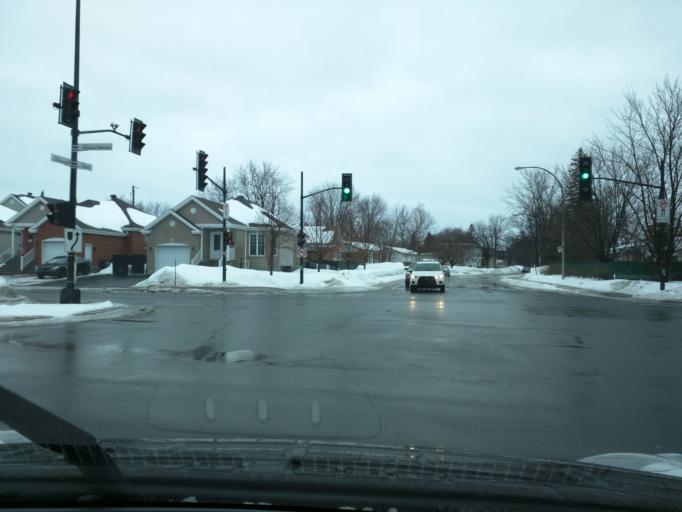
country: CA
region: Quebec
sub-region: Monteregie
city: Longueuil
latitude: 45.5304
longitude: -73.4576
